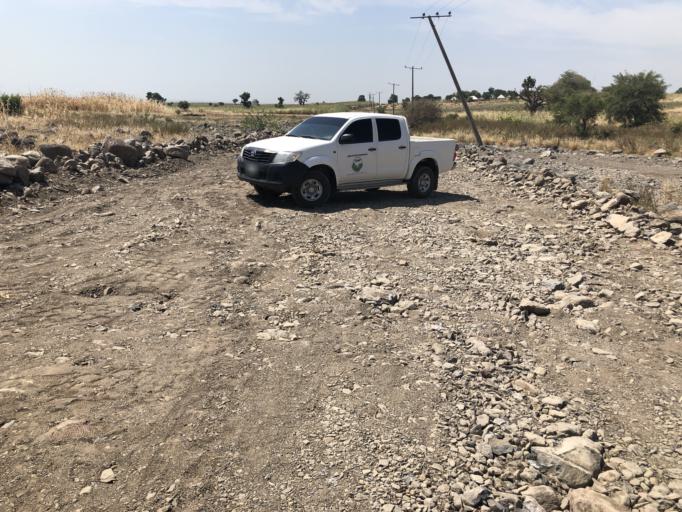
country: NG
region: Adamawa
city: Numan
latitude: 9.6900
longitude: 11.9124
